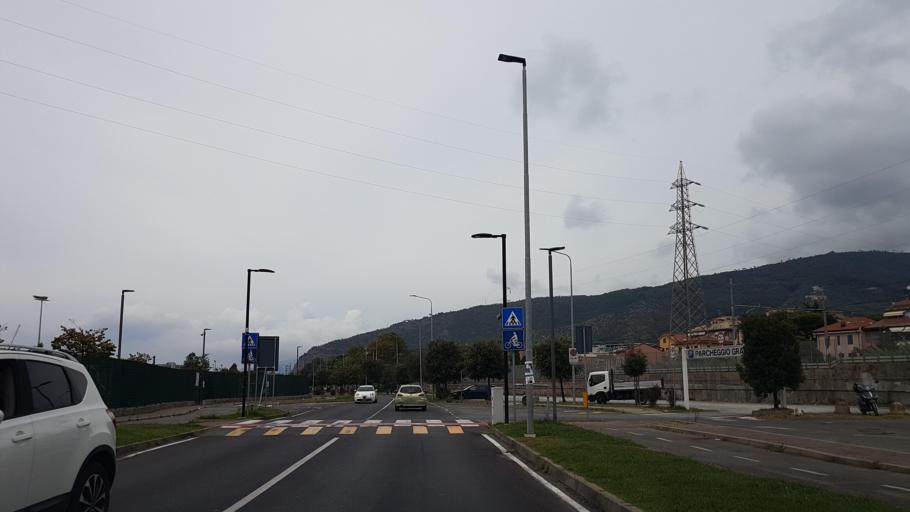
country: IT
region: Liguria
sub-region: Provincia di Genova
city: Sestri Levante
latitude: 44.2709
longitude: 9.4086
